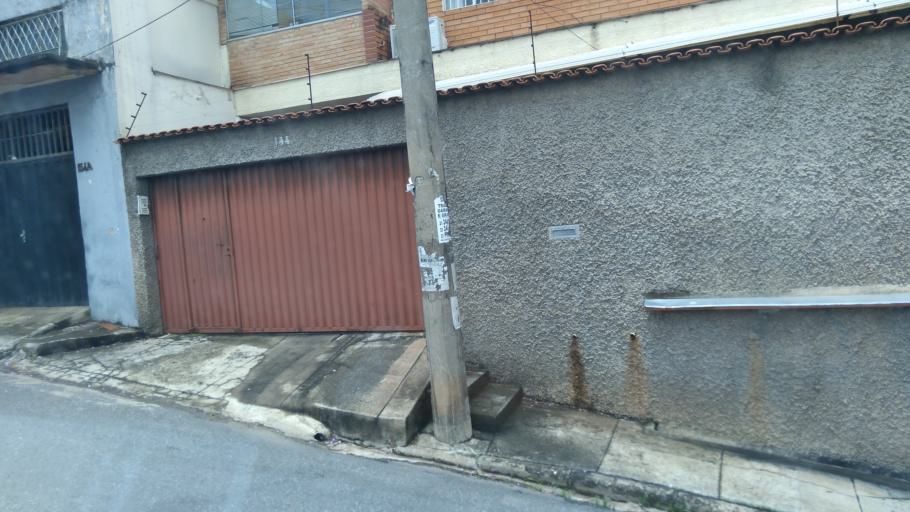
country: BR
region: Minas Gerais
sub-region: Belo Horizonte
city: Belo Horizonte
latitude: -19.9206
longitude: -43.9096
